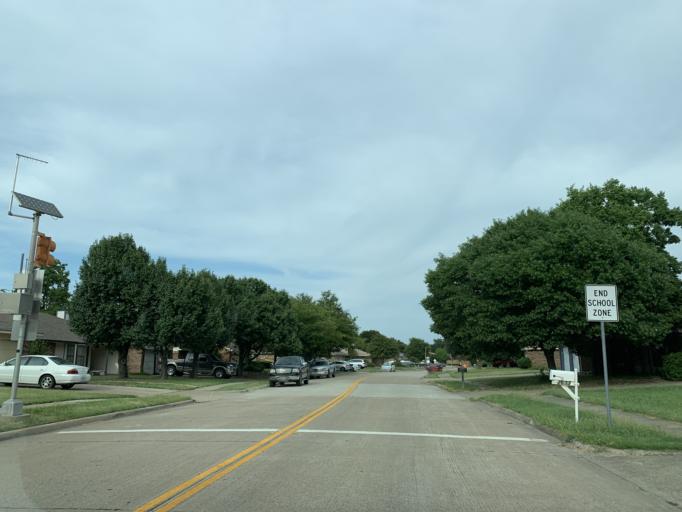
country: US
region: Texas
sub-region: Dallas County
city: Grand Prairie
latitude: 32.6654
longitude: -97.0457
